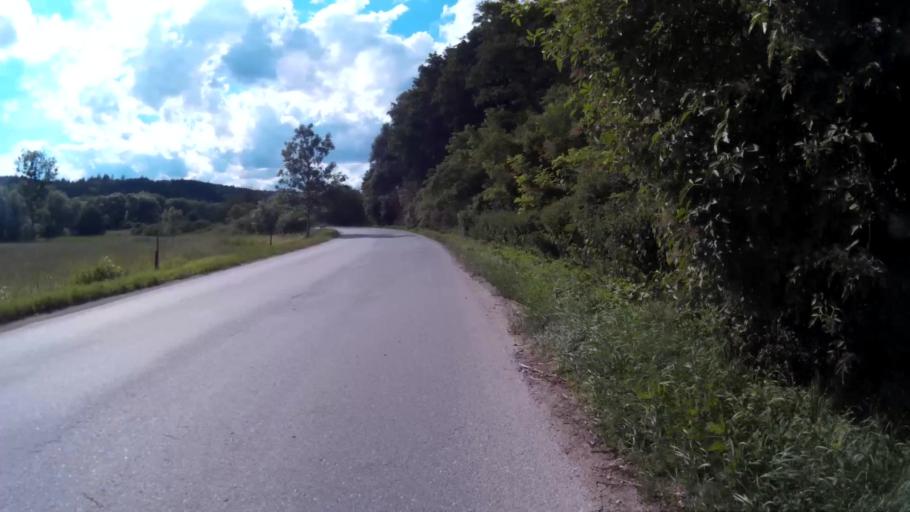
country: CZ
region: South Moravian
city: Strelice
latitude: 49.1538
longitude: 16.4564
